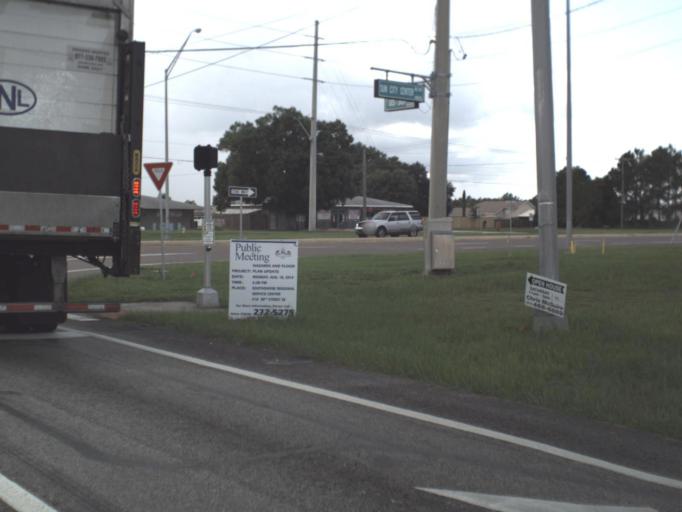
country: US
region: Florida
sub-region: Hillsborough County
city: Sun City Center
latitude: 27.7129
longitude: -82.3353
